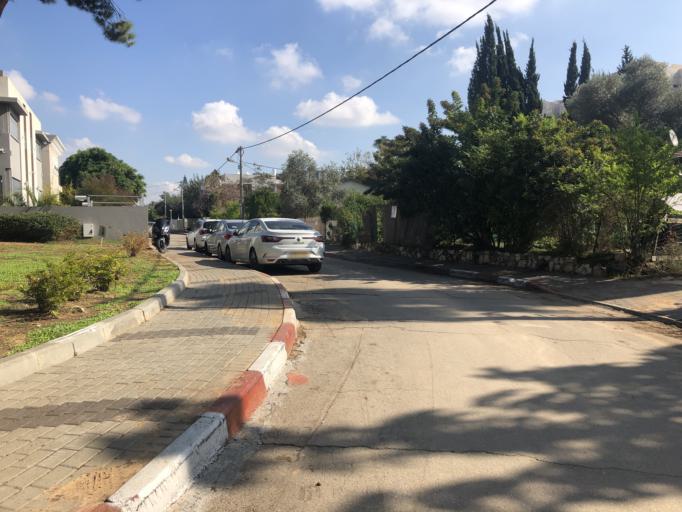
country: IL
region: Tel Aviv
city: Or Yehuda
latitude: 32.0282
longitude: 34.8681
